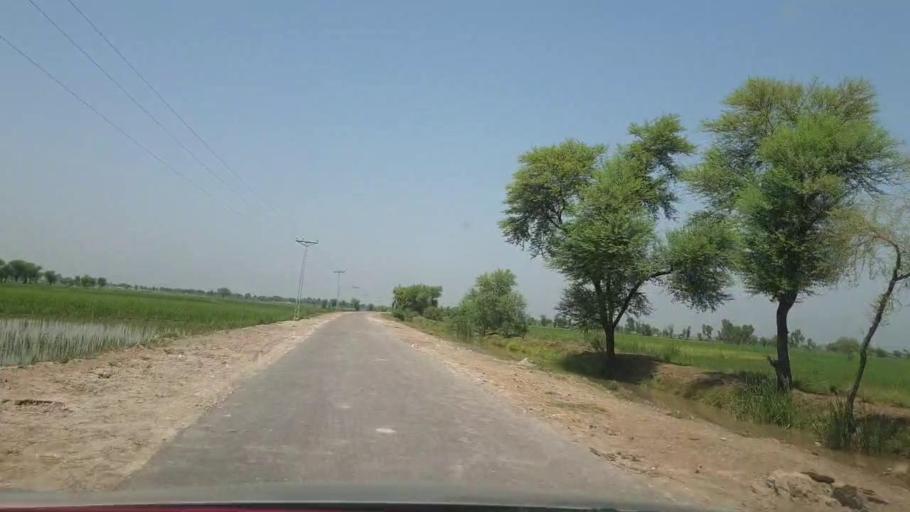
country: PK
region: Sindh
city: Warah
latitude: 27.4724
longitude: 67.7622
